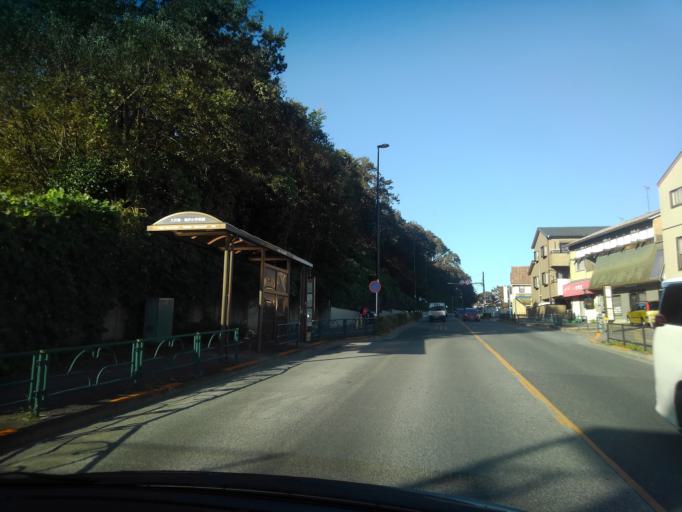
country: JP
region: Tokyo
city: Chofugaoka
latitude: 35.6718
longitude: 139.5386
